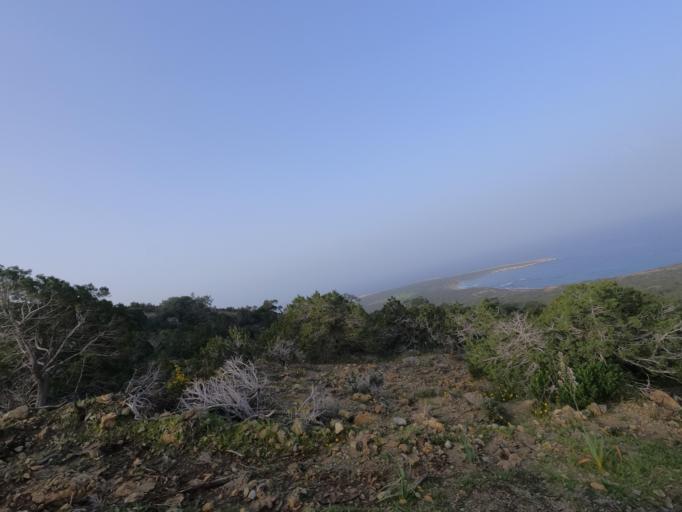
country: CY
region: Pafos
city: Pegeia
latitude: 34.9672
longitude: 32.3248
